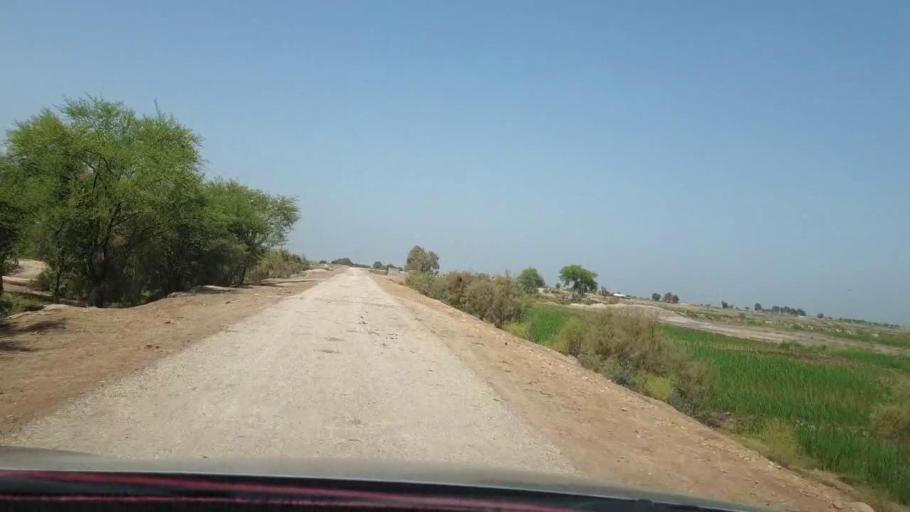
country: PK
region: Sindh
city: Warah
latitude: 27.5192
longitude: 67.7086
